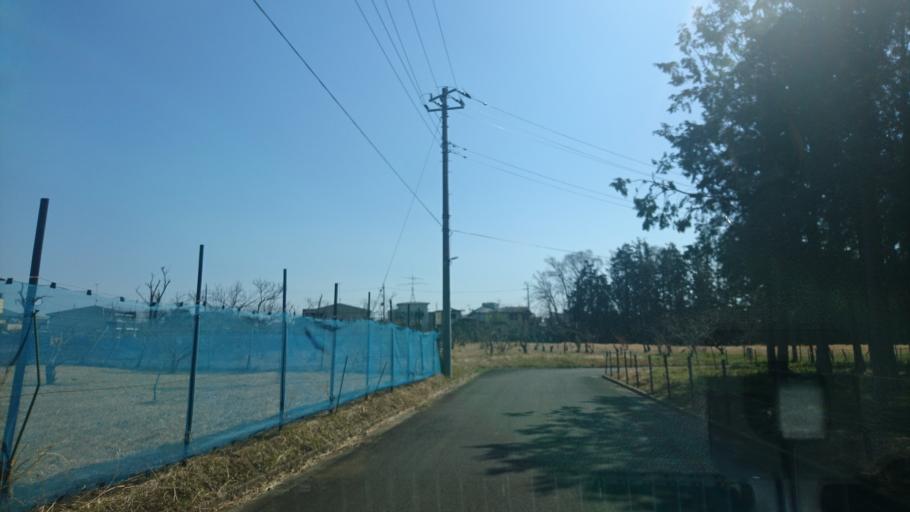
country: JP
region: Kanagawa
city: Fujisawa
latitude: 35.3975
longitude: 139.4370
